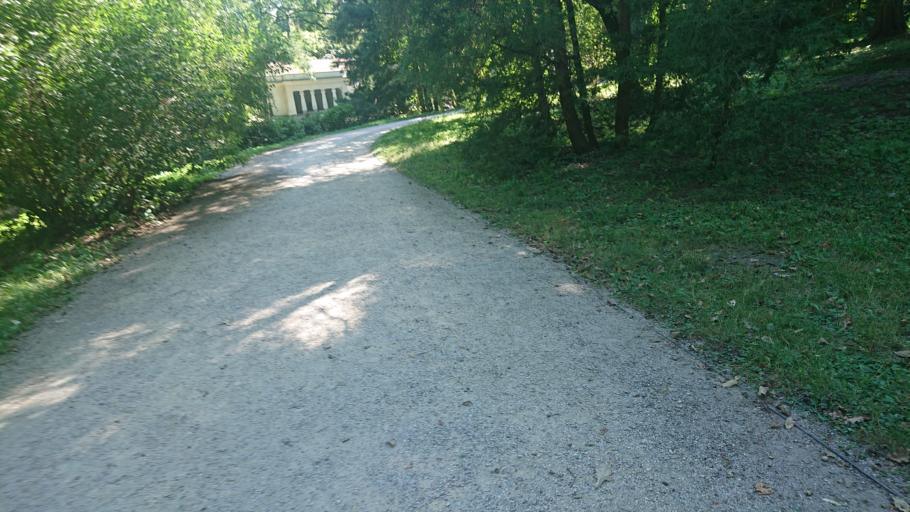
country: PL
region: Masovian Voivodeship
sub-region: Warszawa
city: Mokotow
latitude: 52.2121
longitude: 21.0292
